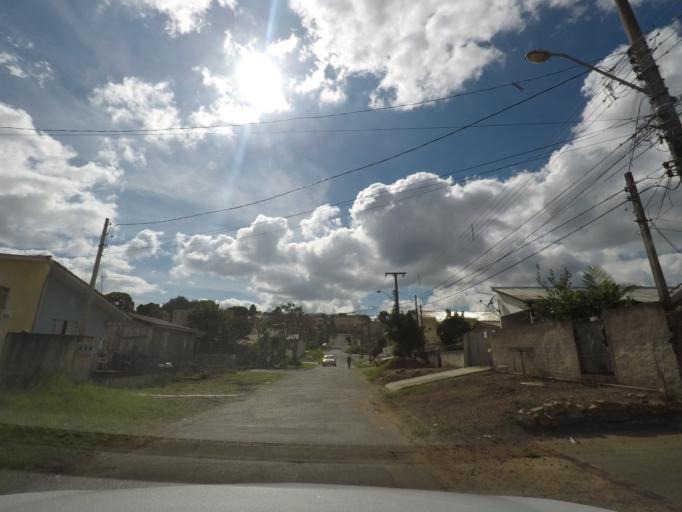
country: BR
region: Parana
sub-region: Sao Jose Dos Pinhais
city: Sao Jose dos Pinhais
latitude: -25.4872
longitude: -49.2325
